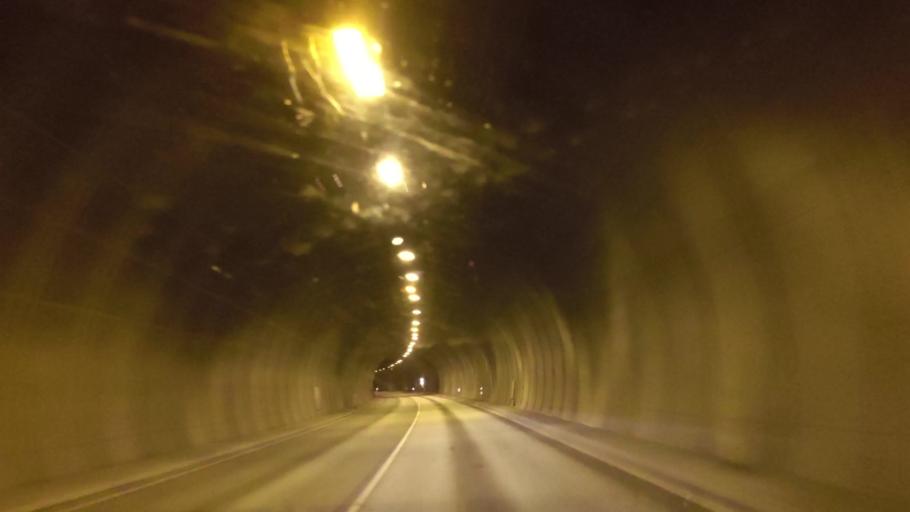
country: IS
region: Capital Region
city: Reykjavik
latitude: 64.2868
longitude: -21.8470
